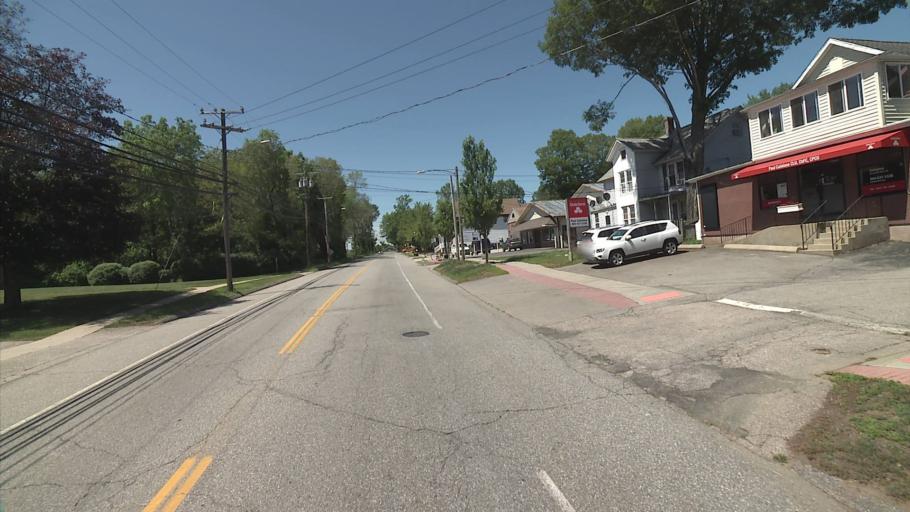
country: US
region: Connecticut
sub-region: New London County
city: Colchester
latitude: 41.5778
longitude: -72.3296
